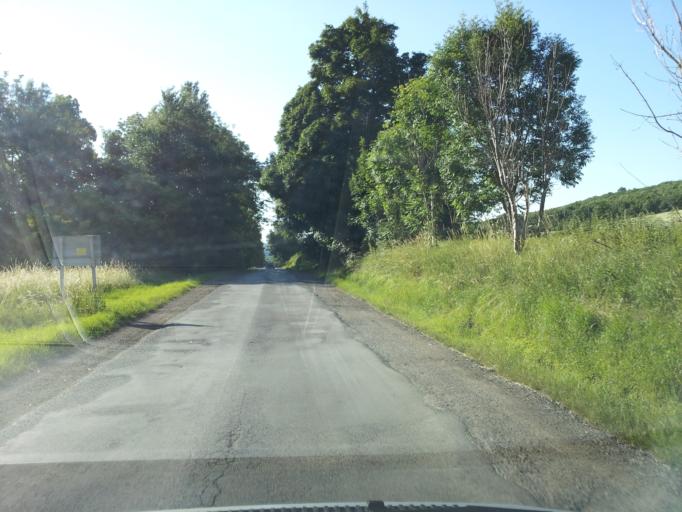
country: HU
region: Veszprem
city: Zirc
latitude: 47.2072
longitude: 17.8489
